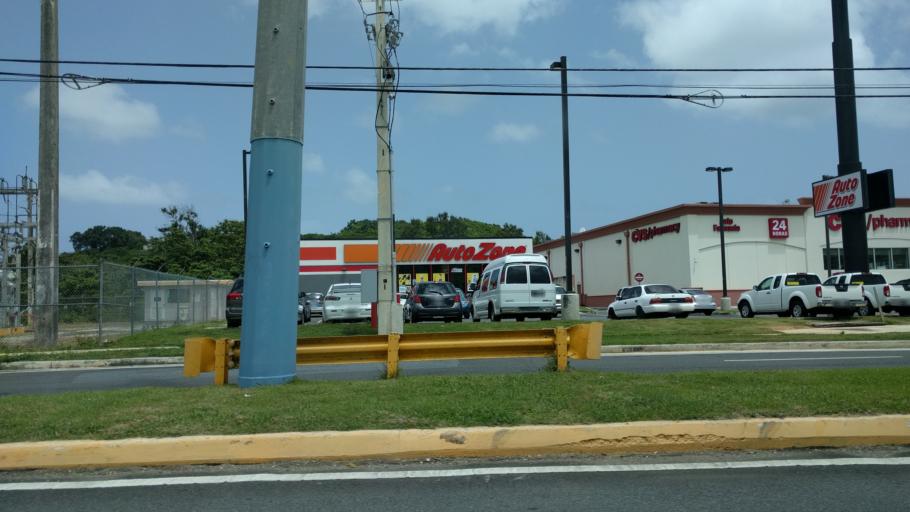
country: PR
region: Manati
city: Manati
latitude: 18.4327
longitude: -66.4857
